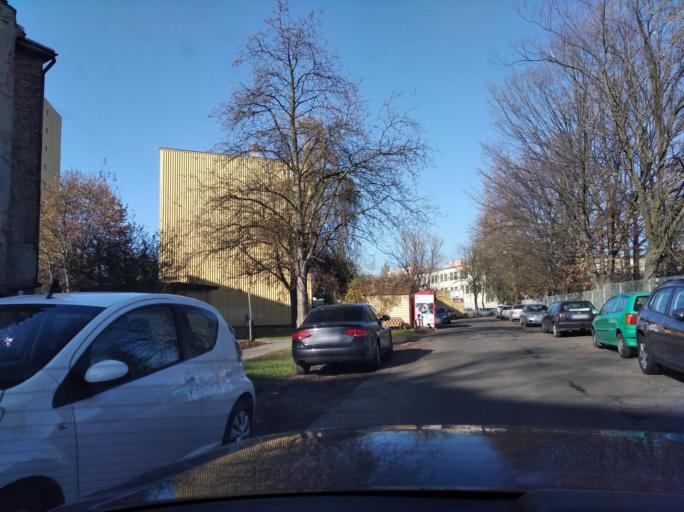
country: PL
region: Subcarpathian Voivodeship
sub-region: Rzeszow
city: Rzeszow
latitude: 50.0319
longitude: 21.9900
